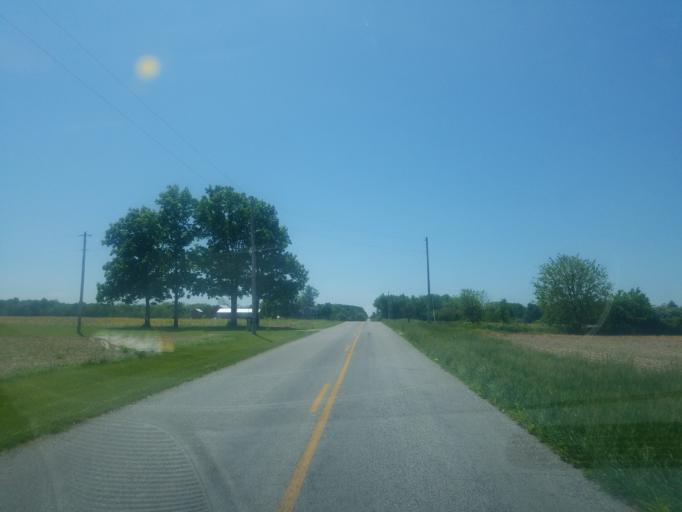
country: US
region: Ohio
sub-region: Huron County
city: New London
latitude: 41.1532
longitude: -82.3796
